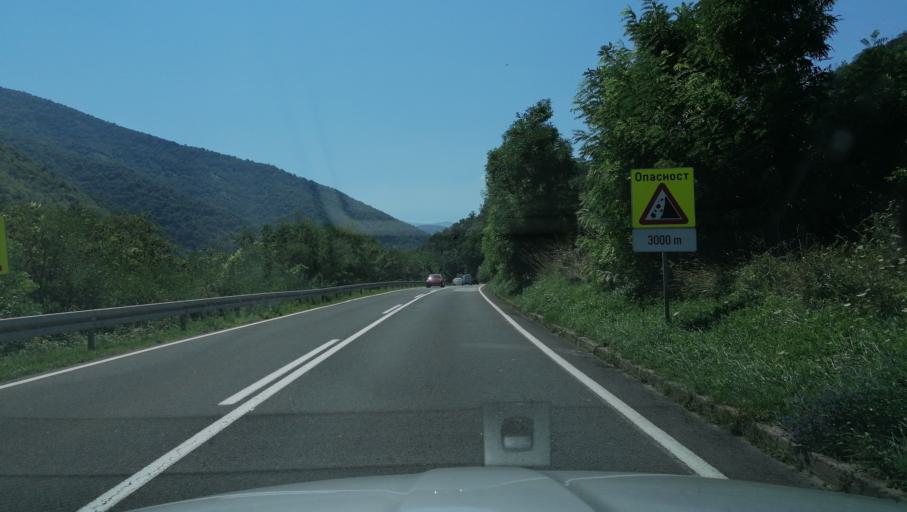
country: RS
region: Central Serbia
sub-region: Raski Okrug
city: Kraljevo
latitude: 43.6443
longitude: 20.5520
